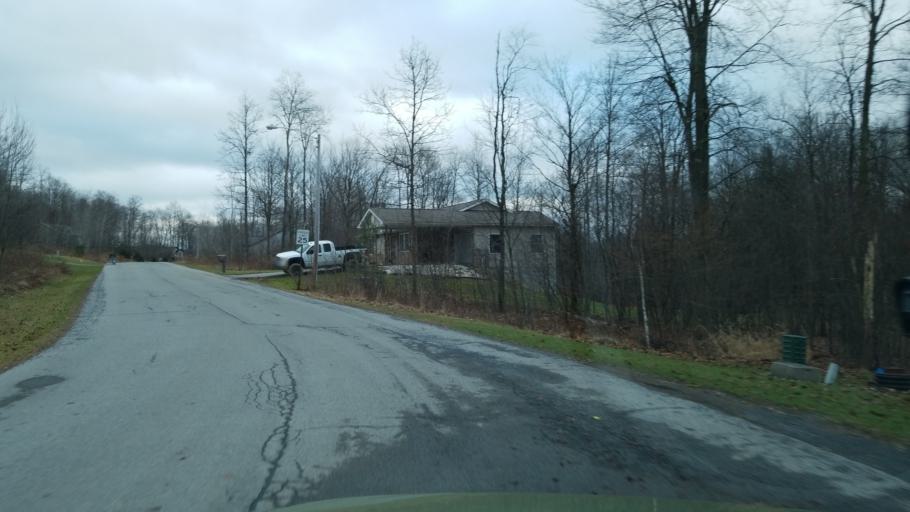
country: US
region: Pennsylvania
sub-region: Jefferson County
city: Falls Creek
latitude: 41.1382
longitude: -78.8105
